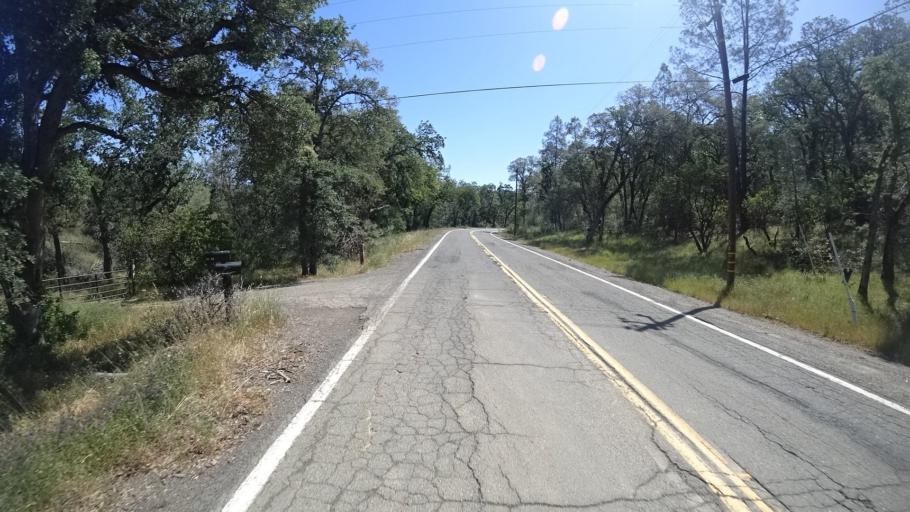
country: US
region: California
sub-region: Lake County
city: Hidden Valley Lake
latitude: 38.8773
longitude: -122.4298
